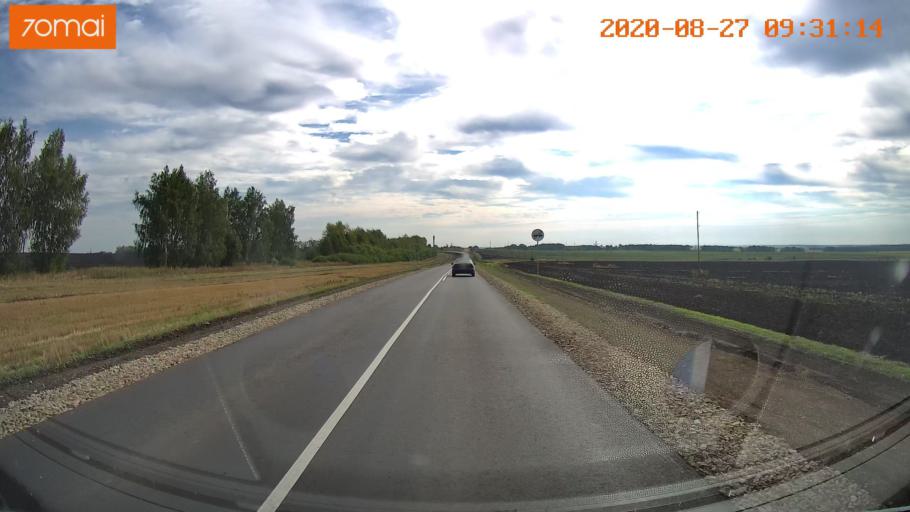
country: RU
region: Tula
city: Kazachka
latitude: 53.3168
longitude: 38.2550
